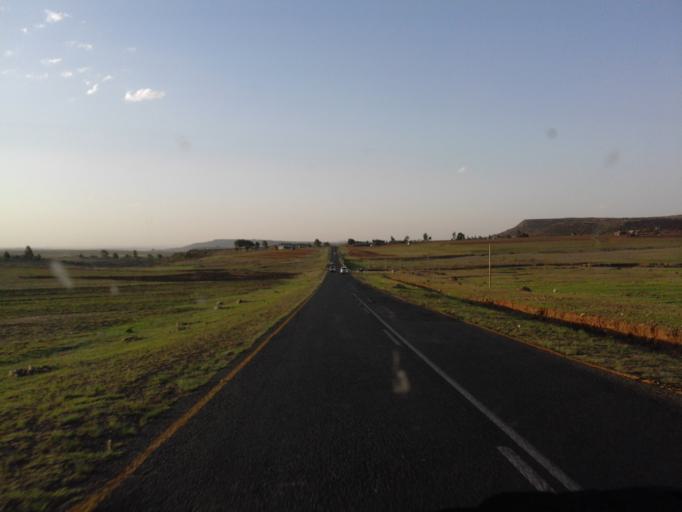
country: LS
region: Mafeteng
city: Mafeteng
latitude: -29.8887
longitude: 27.2516
